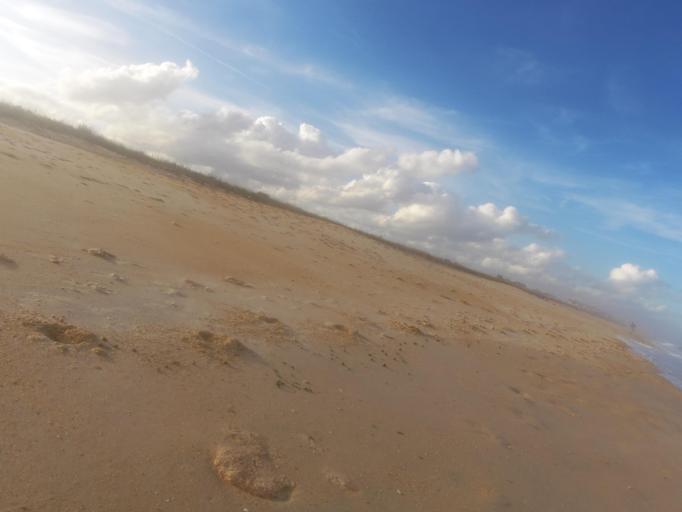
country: US
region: Florida
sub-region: Flagler County
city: Palm Coast
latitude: 29.6173
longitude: -81.1900
